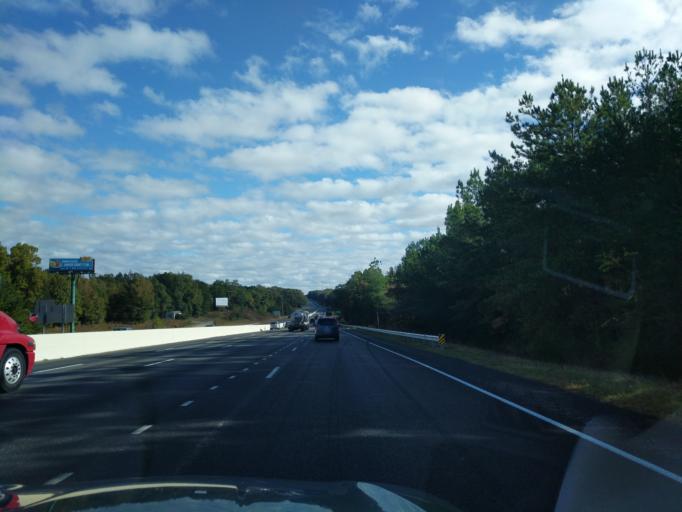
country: US
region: South Carolina
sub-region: Spartanburg County
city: Wellford
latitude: 34.9176
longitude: -82.1014
